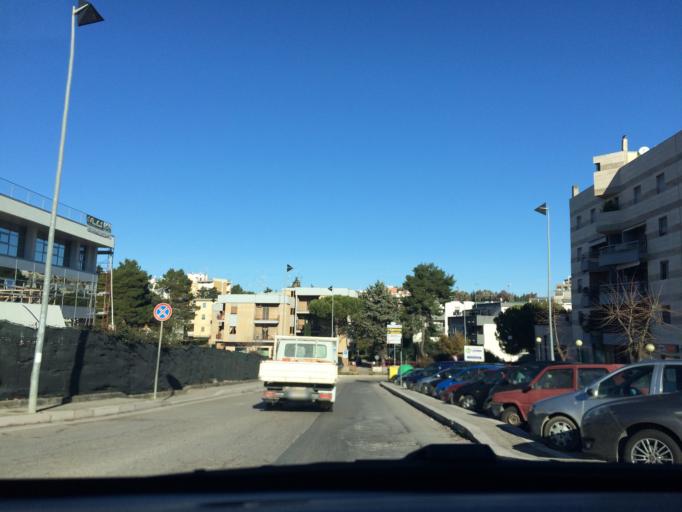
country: IT
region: Basilicate
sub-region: Provincia di Matera
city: Matera
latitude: 40.6629
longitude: 16.5970
